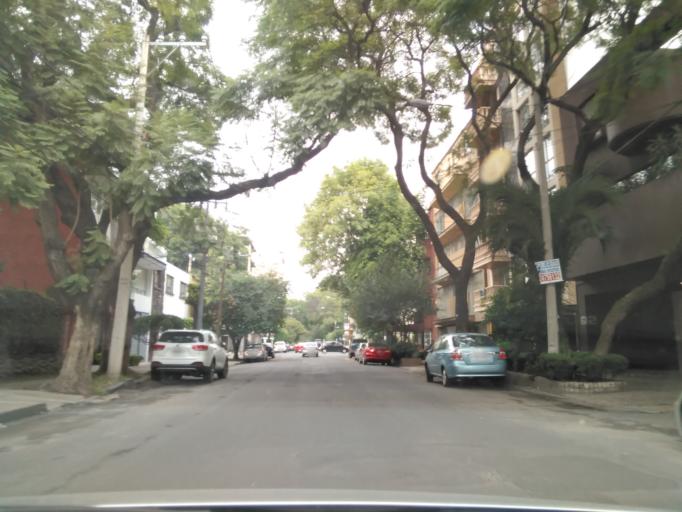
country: MX
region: Mexico City
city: Colonia del Valle
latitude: 19.3901
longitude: -99.1714
